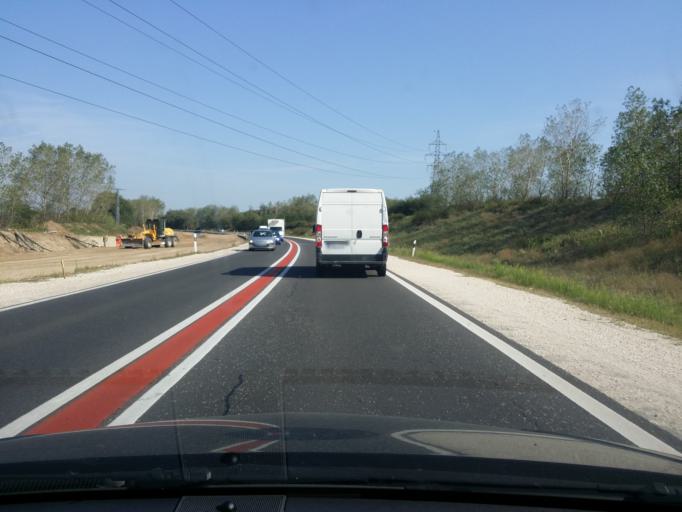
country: HU
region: Pest
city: Fot
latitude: 47.6354
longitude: 19.1698
